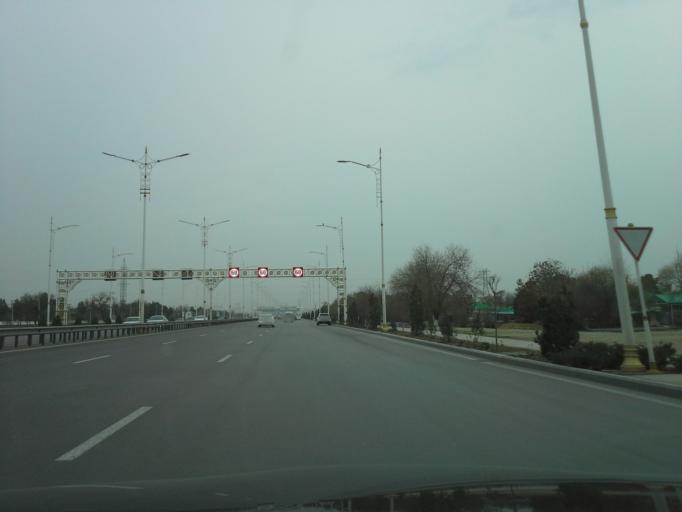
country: TM
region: Ahal
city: Ashgabat
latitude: 37.9693
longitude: 58.3535
